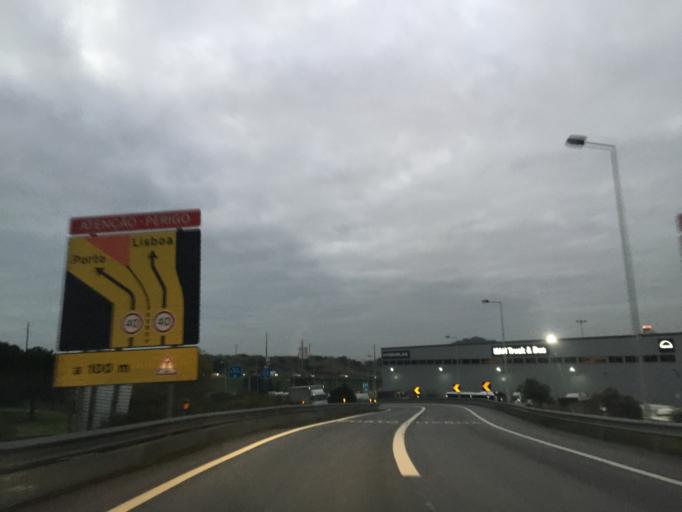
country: PT
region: Lisbon
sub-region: Vila Franca de Xira
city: Vialonga
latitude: 38.8946
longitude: -9.0504
